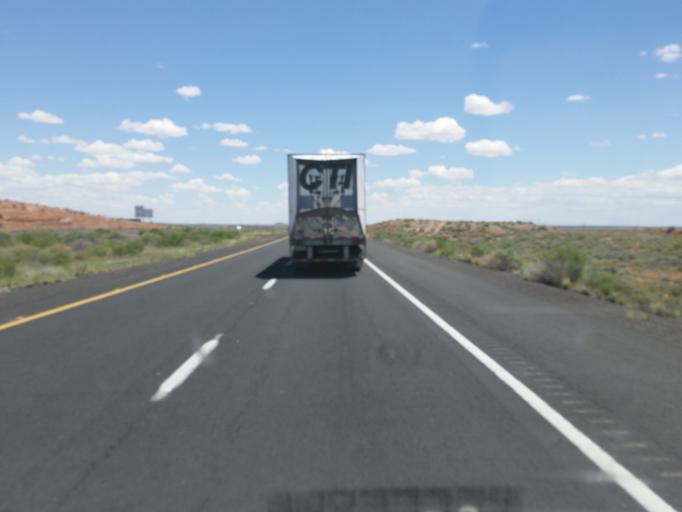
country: US
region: Arizona
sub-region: Navajo County
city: Holbrook
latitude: 34.9146
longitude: -110.2483
